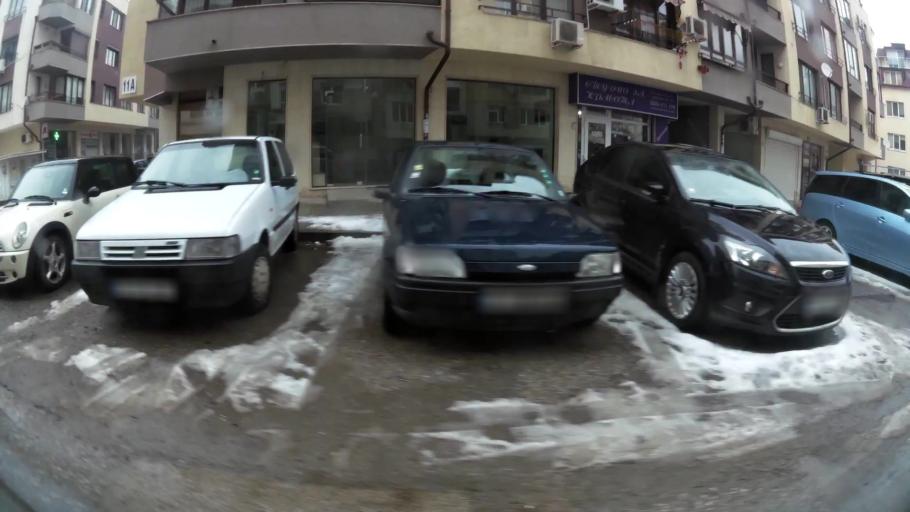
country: BG
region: Sofia-Capital
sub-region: Stolichna Obshtina
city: Sofia
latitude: 42.6613
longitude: 23.2919
